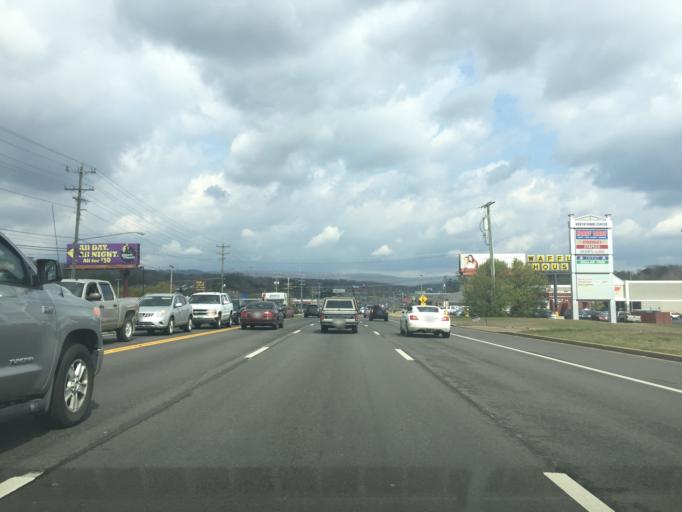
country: US
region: Tennessee
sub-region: Hamilton County
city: Red Bank
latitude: 35.1387
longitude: -85.2478
